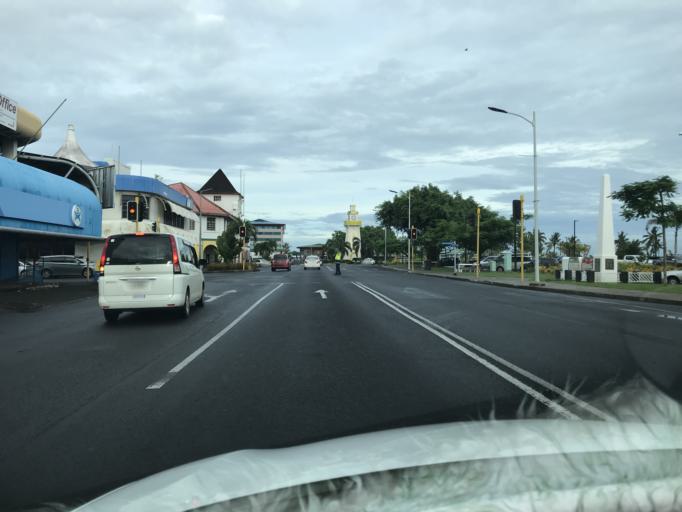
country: WS
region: Tuamasaga
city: Apia
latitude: -13.8311
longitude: -171.7674
